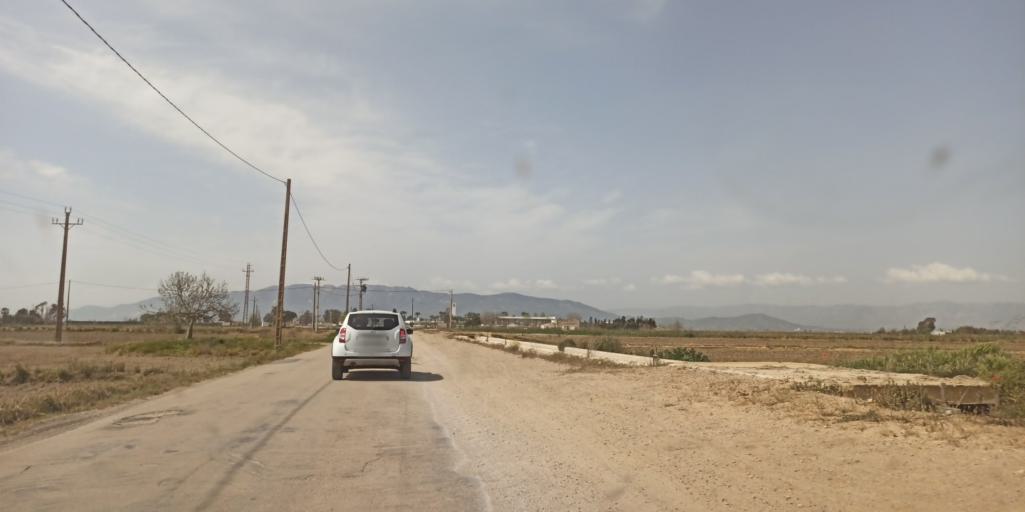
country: ES
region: Catalonia
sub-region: Provincia de Tarragona
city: Deltebre
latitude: 40.6460
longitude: 0.6962
